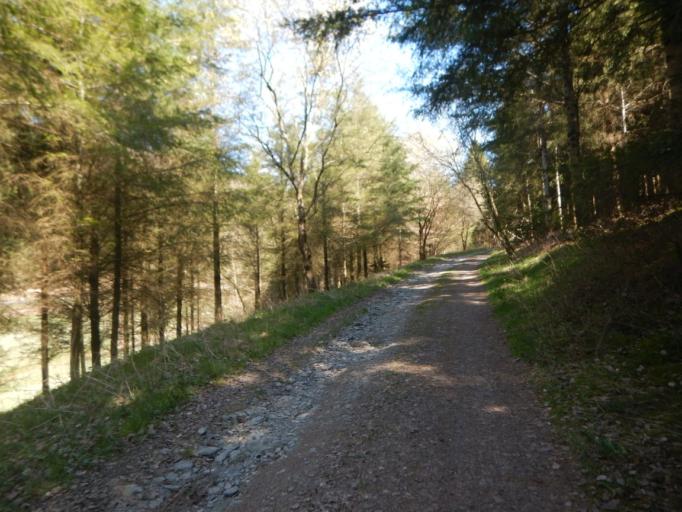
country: LU
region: Diekirch
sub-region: Canton de Clervaux
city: Troisvierges
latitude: 50.0982
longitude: 6.0290
